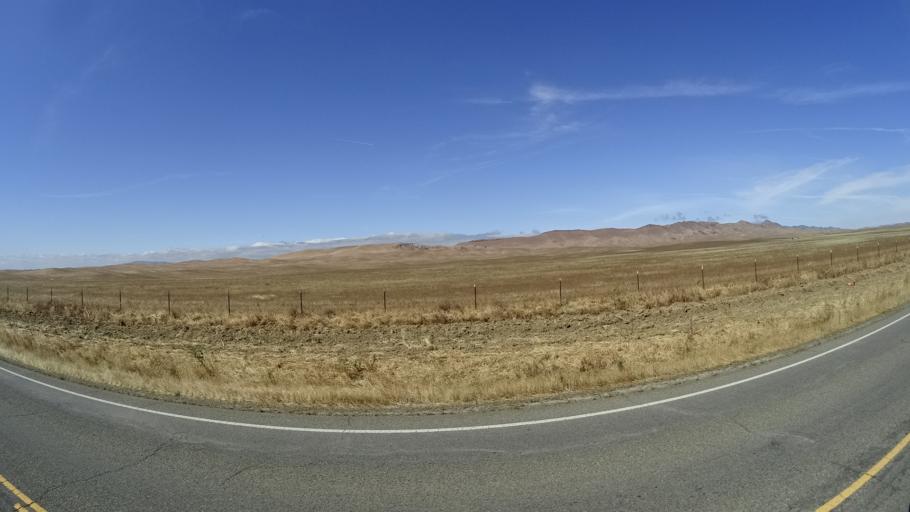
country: US
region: California
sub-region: Kings County
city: Avenal
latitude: 35.9229
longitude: -120.0747
